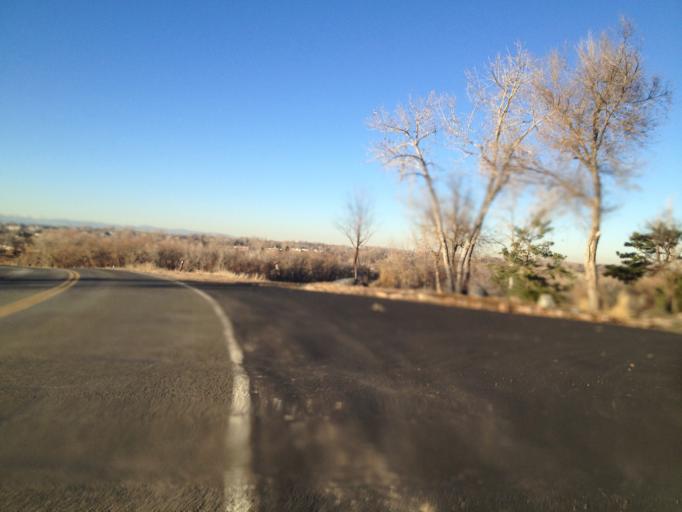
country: US
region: Colorado
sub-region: Boulder County
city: Louisville
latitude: 39.9752
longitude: -105.1093
